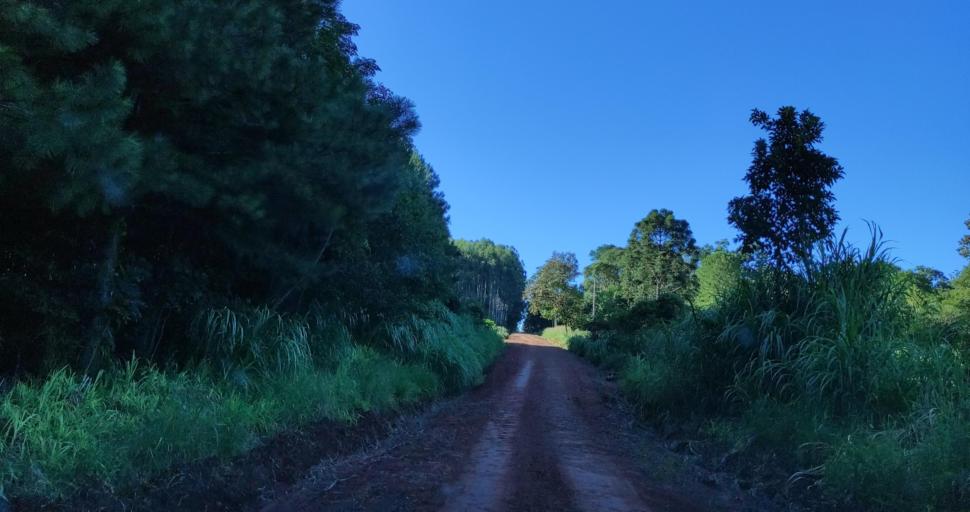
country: AR
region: Misiones
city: Garuhape
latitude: -26.8628
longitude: -55.0046
